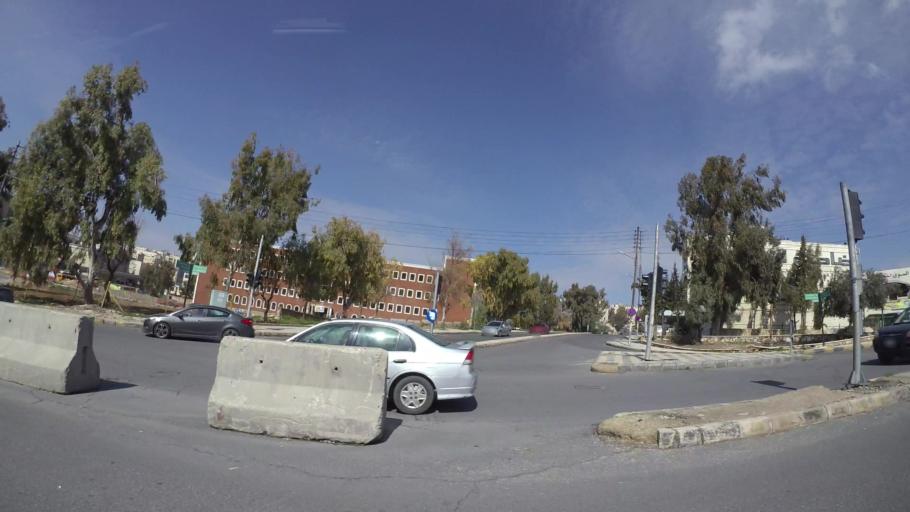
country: JO
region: Amman
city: Al Jubayhah
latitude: 31.9935
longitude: 35.8912
